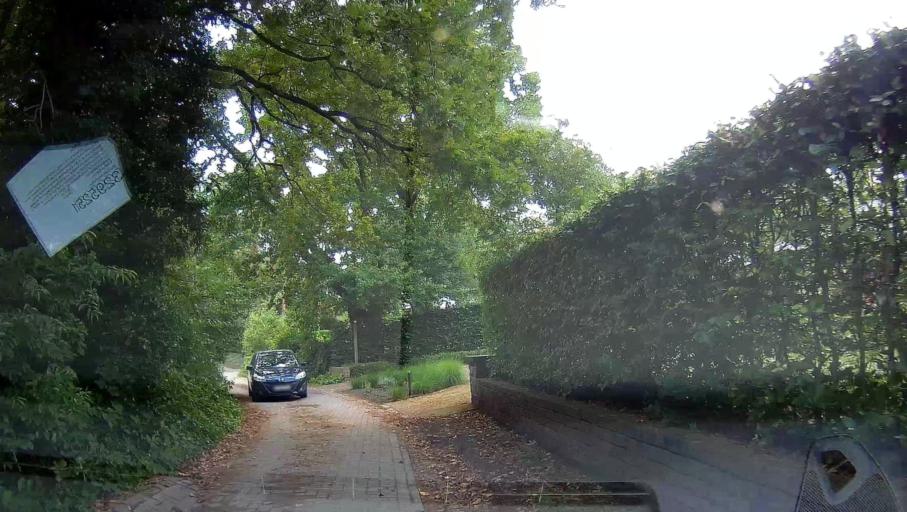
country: BE
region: Flanders
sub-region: Provincie Antwerpen
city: Mol
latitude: 51.1956
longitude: 5.1018
